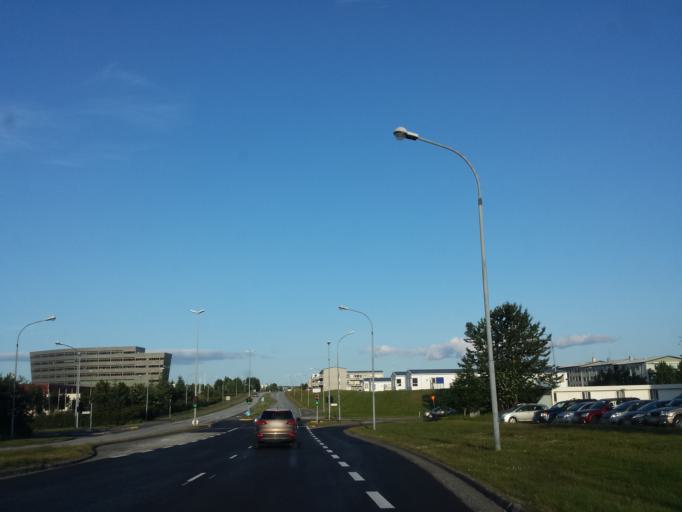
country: IS
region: Capital Region
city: Reykjavik
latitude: 64.1206
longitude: -21.8092
